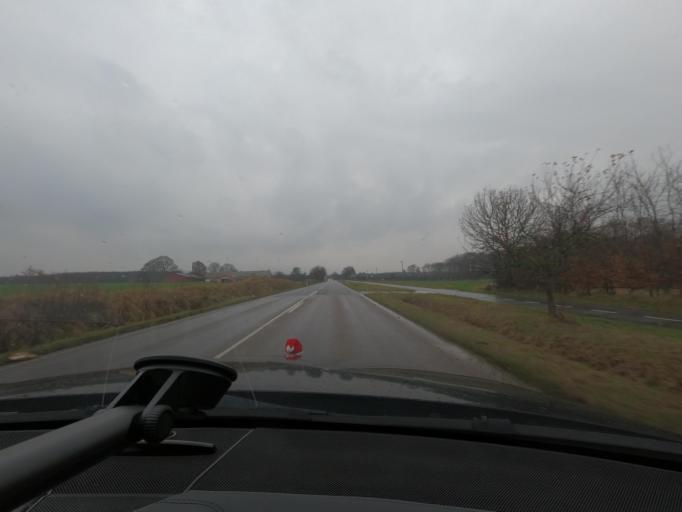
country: DK
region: South Denmark
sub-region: Sonderborg Kommune
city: Horuphav
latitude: 54.9051
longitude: 9.8662
